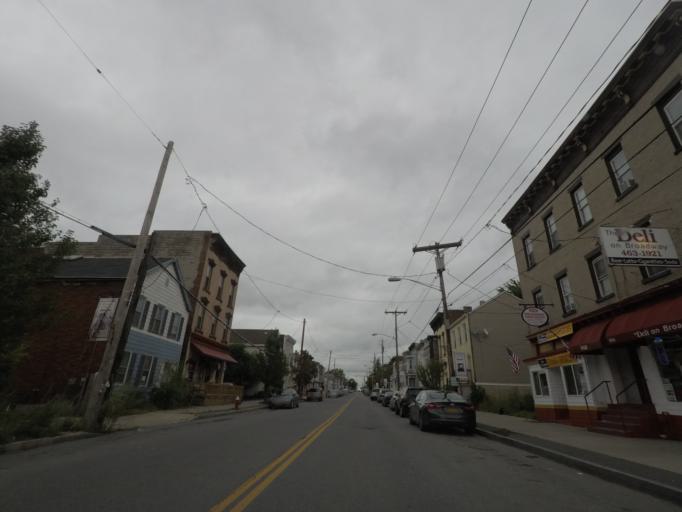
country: US
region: New York
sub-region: Rensselaer County
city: Rensselaer
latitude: 42.6474
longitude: -73.7391
